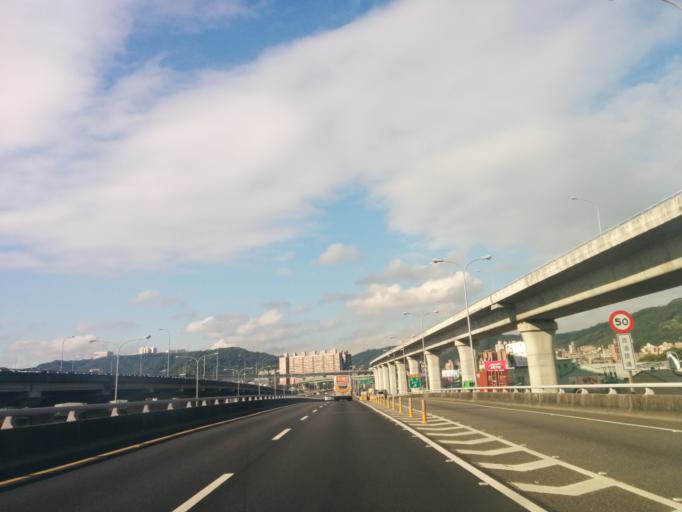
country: TW
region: Taipei
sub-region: Taipei
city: Banqiao
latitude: 25.0711
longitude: 121.4456
